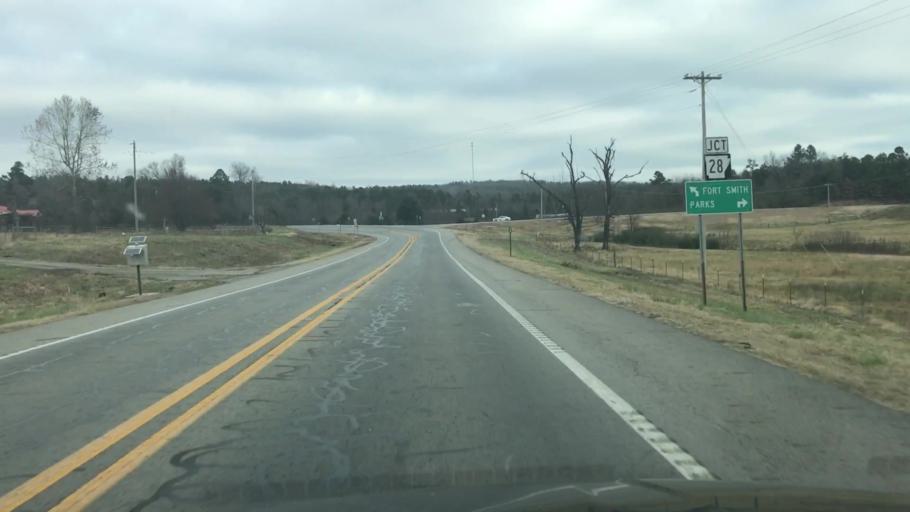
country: US
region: Arkansas
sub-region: Scott County
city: Waldron
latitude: 34.8065
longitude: -94.0399
